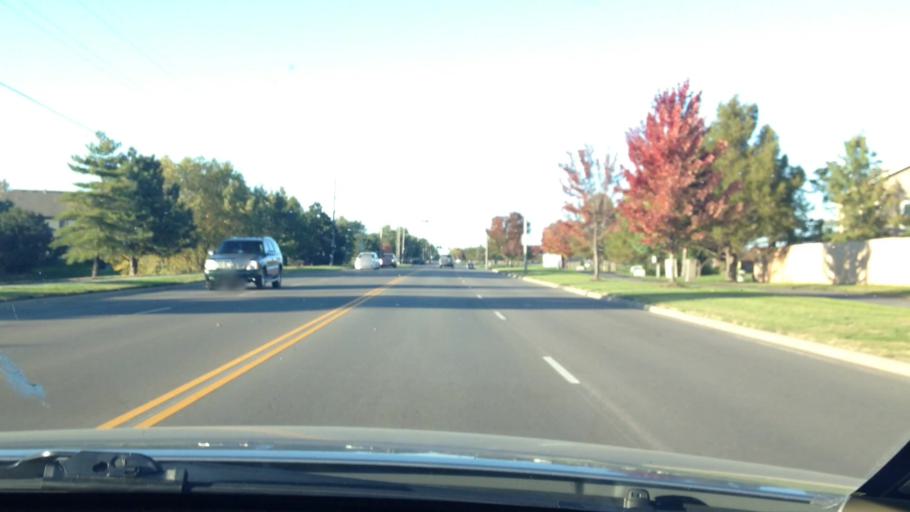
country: US
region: Kansas
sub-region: Johnson County
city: Gardner
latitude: 38.7933
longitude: -94.9276
